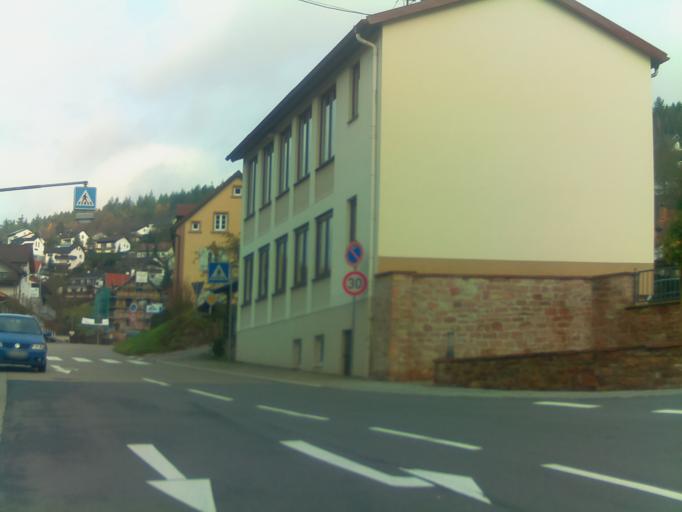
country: DE
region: Baden-Wuerttemberg
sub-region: Karlsruhe Region
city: Heiligkreuzsteinach
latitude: 49.4855
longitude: 8.7971
